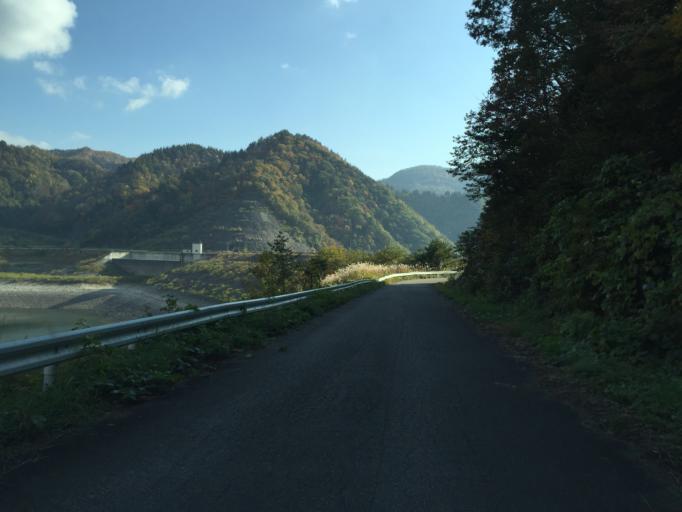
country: JP
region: Fukushima
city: Kitakata
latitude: 37.7557
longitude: 139.9078
